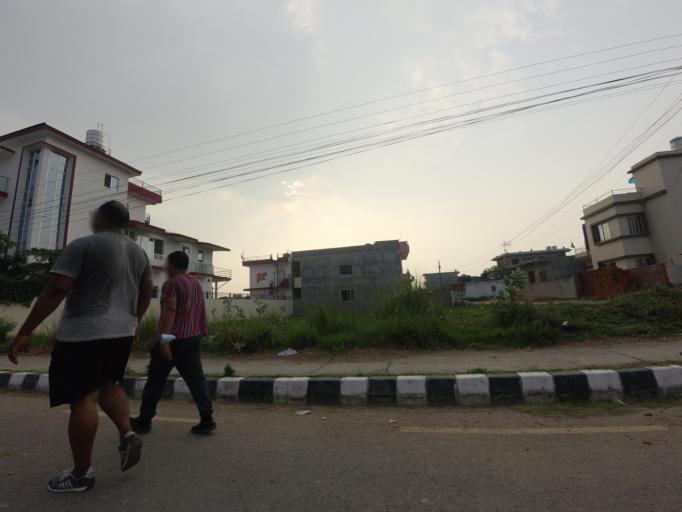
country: NP
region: Western Region
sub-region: Lumbini Zone
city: Bhairahawa
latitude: 27.5021
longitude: 83.4439
